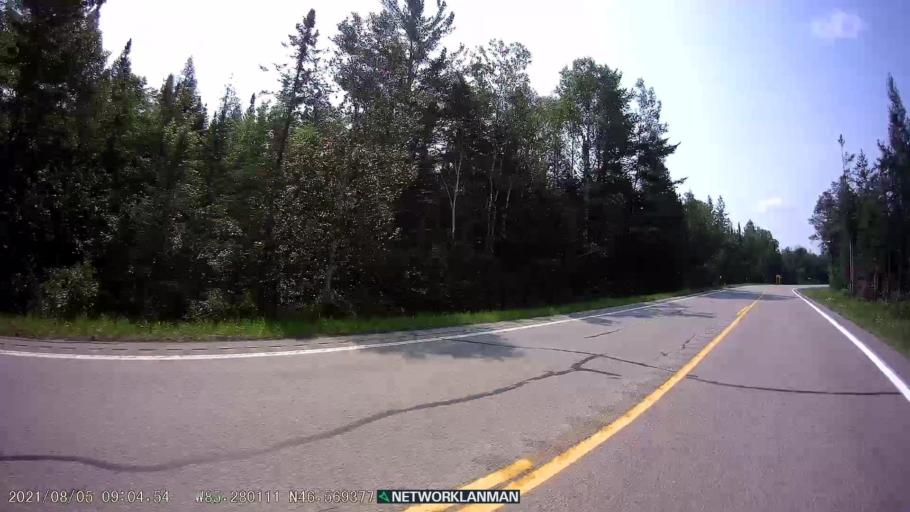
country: US
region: Michigan
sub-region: Luce County
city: Newberry
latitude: 46.5692
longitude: -85.2804
